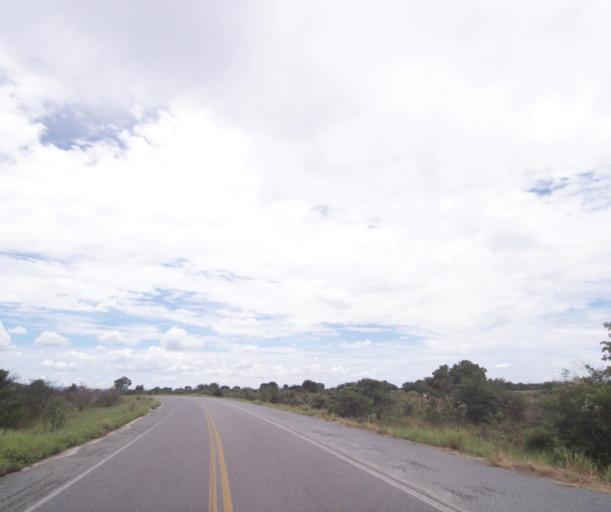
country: BR
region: Bahia
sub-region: Carinhanha
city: Carinhanha
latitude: -14.3147
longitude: -43.7849
